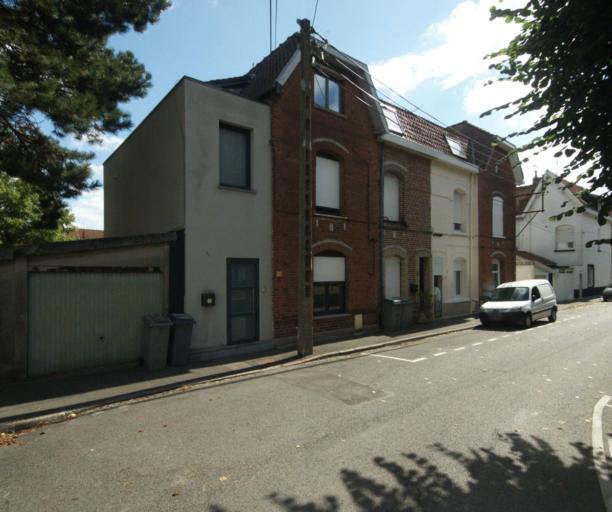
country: FR
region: Nord-Pas-de-Calais
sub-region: Departement du Nord
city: Wasquehal
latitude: 50.6785
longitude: 3.1329
